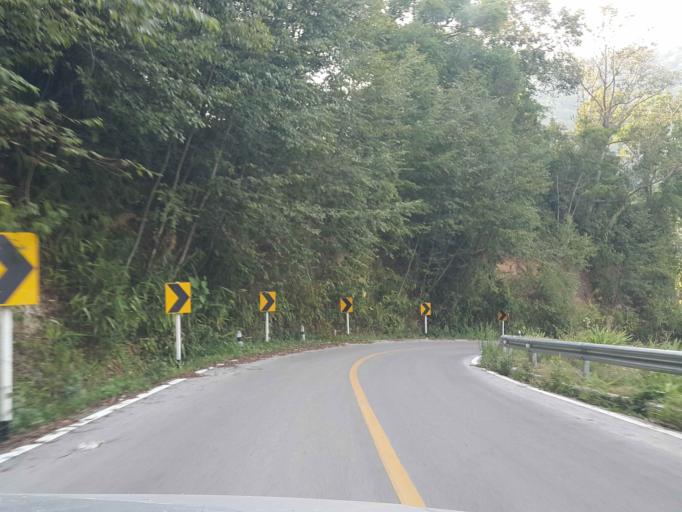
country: TH
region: Chiang Mai
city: Mae On
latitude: 18.9442
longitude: 99.3559
